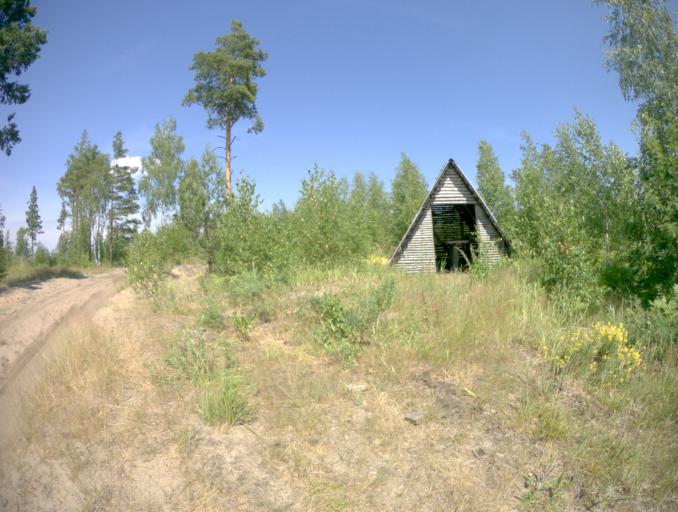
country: RU
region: Ivanovo
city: Talitsy
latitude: 56.4703
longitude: 42.2238
